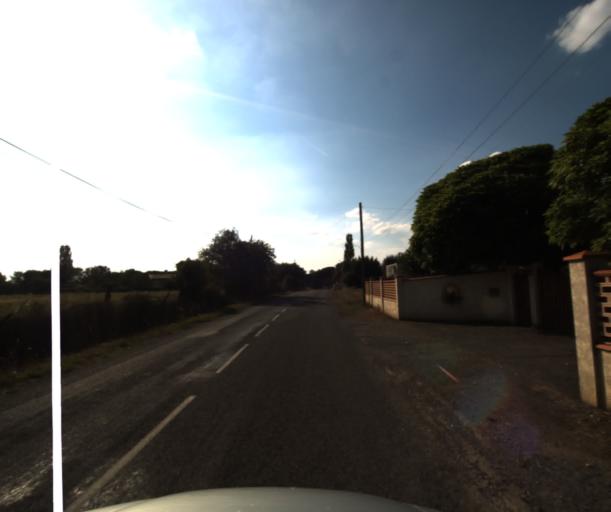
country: FR
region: Midi-Pyrenees
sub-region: Departement de la Haute-Garonne
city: Saint-Lys
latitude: 43.5064
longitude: 1.1912
